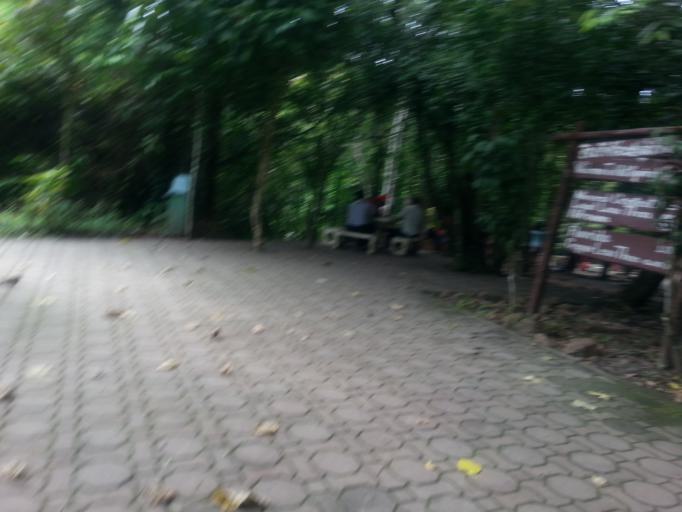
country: TH
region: Krabi
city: Khlong Thom
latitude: 7.9314
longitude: 99.2050
